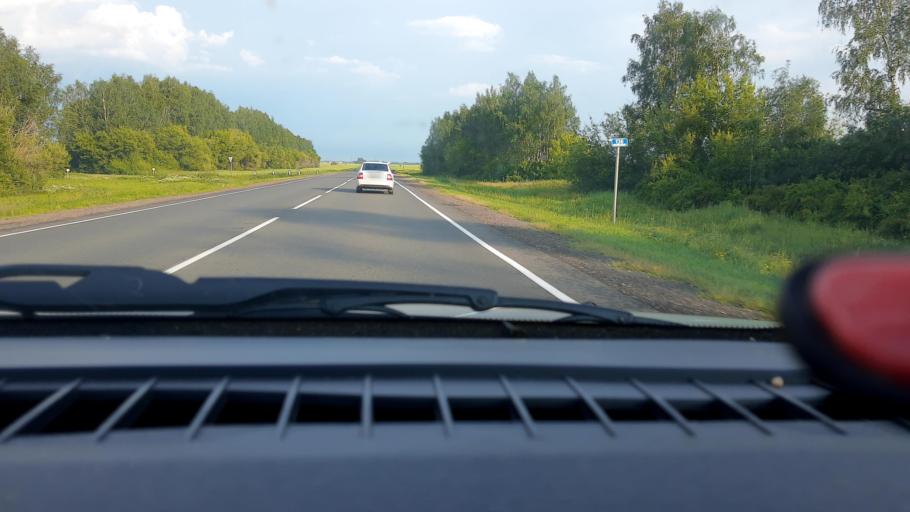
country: RU
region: Nizjnij Novgorod
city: Shatki
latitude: 55.2280
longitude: 44.0656
